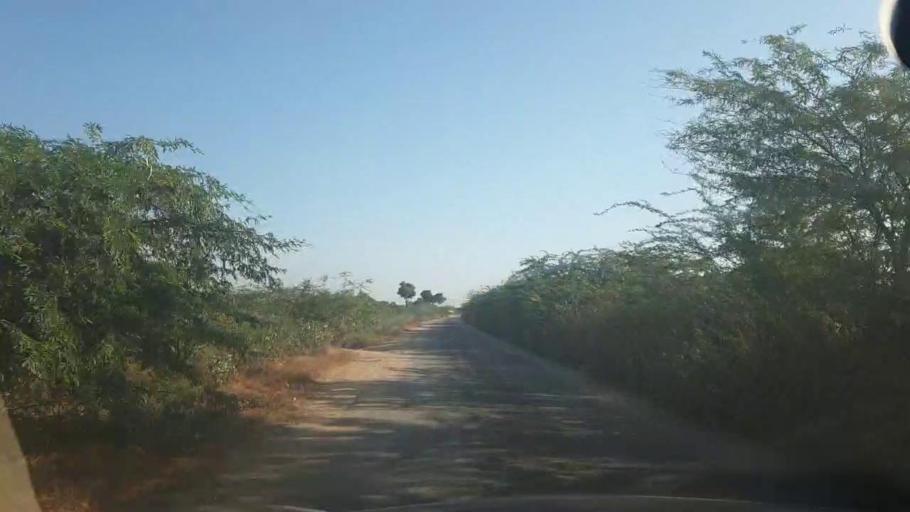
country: PK
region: Sindh
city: Malir Cantonment
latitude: 25.1084
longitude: 67.2634
